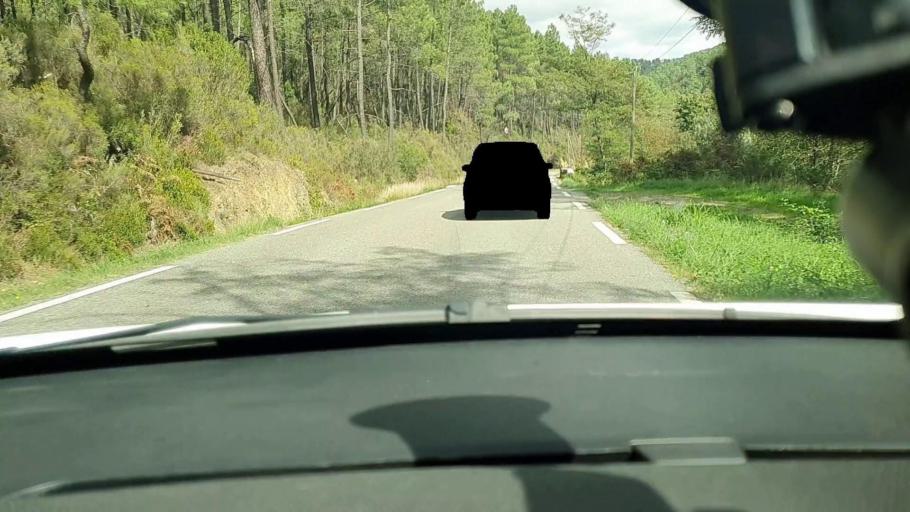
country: FR
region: Languedoc-Roussillon
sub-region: Departement du Gard
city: Les Salles-du-Gardon
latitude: 44.2459
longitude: 4.0530
